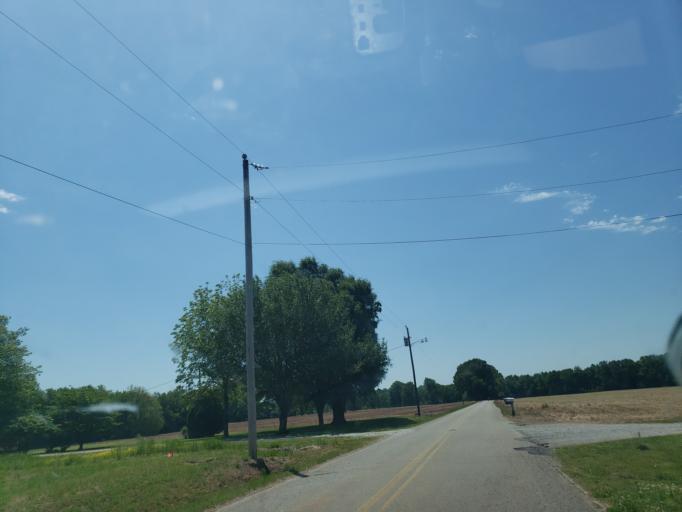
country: US
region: Alabama
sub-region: Madison County
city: Hazel Green
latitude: 34.9464
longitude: -86.5355
